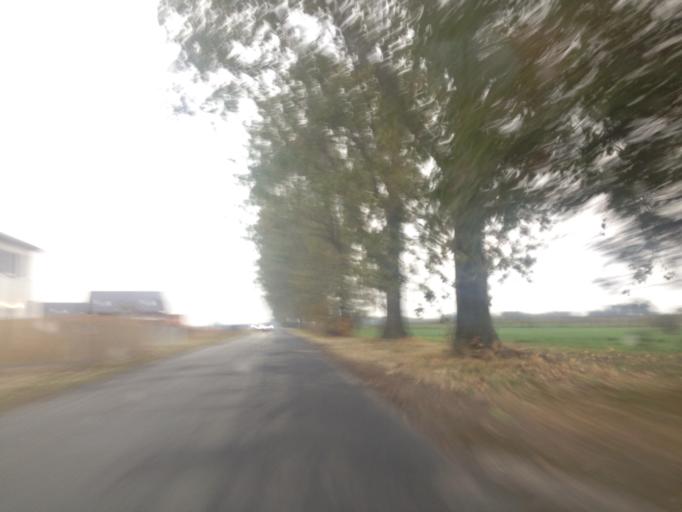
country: PL
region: Greater Poland Voivodeship
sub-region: Powiat poznanski
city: Kleszczewo
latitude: 52.3517
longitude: 17.1465
